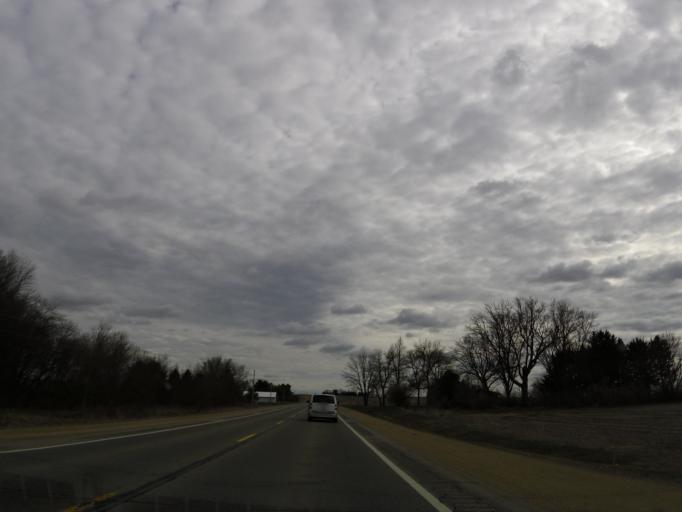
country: US
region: Iowa
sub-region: Chickasaw County
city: New Hampton
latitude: 43.1721
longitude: -92.2988
